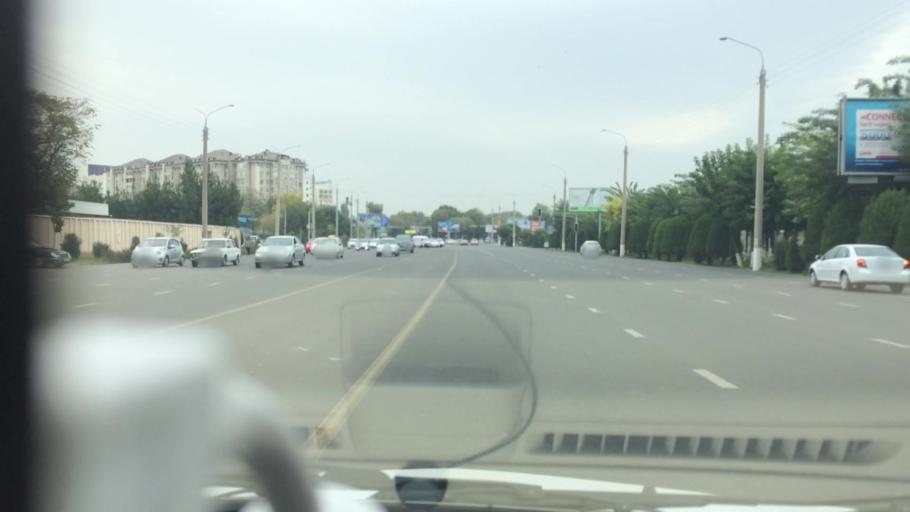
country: UZ
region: Toshkent Shahri
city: Tashkent
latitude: 41.2866
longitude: 69.2805
